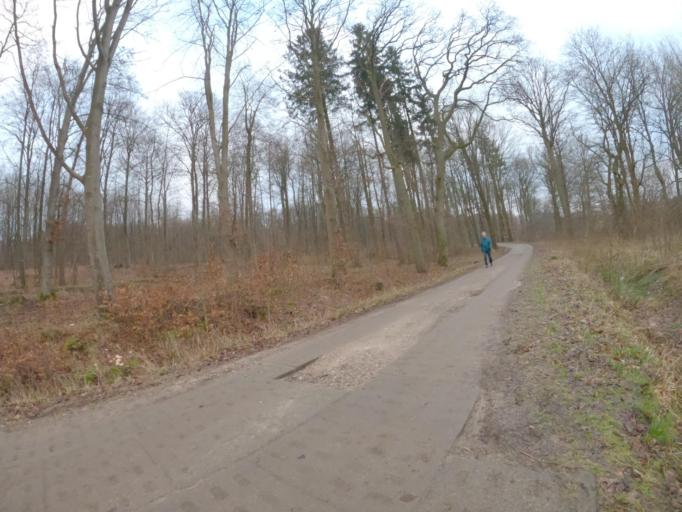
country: PL
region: West Pomeranian Voivodeship
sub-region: Koszalin
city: Koszalin
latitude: 54.2097
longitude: 16.2116
